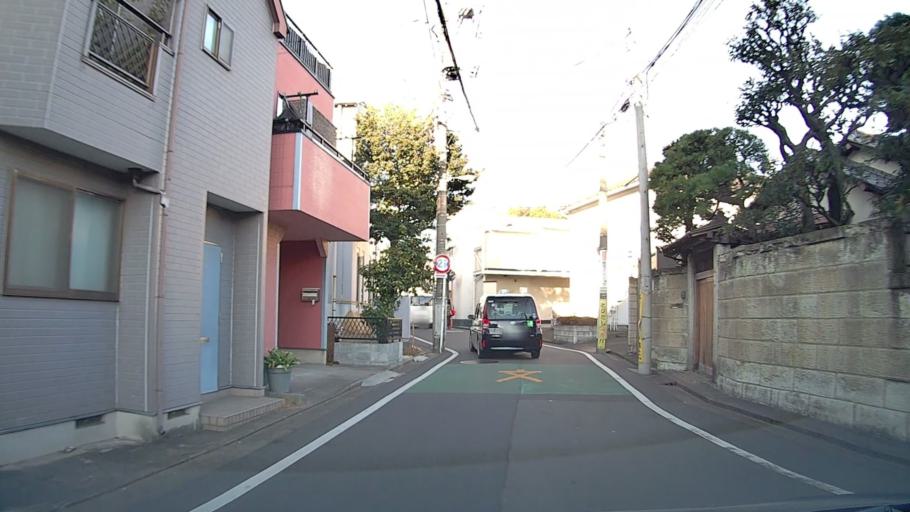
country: JP
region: Tokyo
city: Tokyo
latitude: 35.7116
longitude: 139.6737
